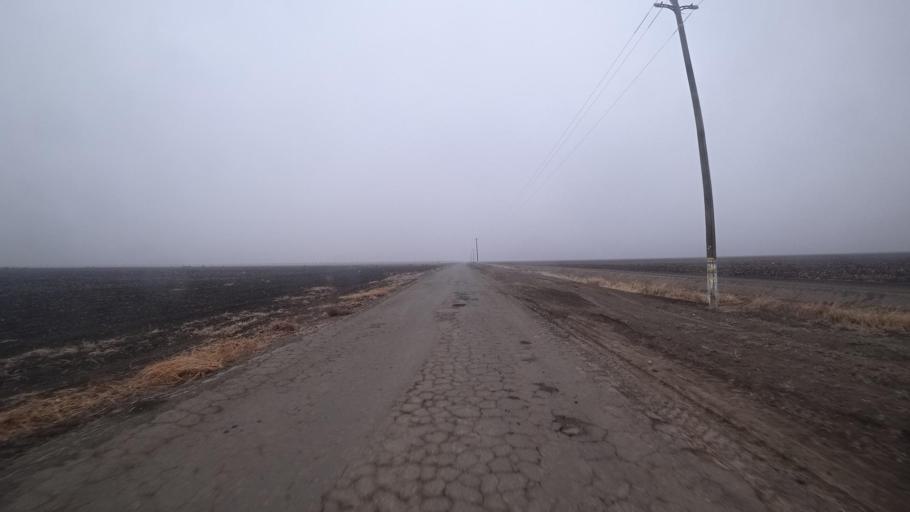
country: US
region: California
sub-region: Kern County
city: Buttonwillow
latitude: 35.4566
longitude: -119.5266
